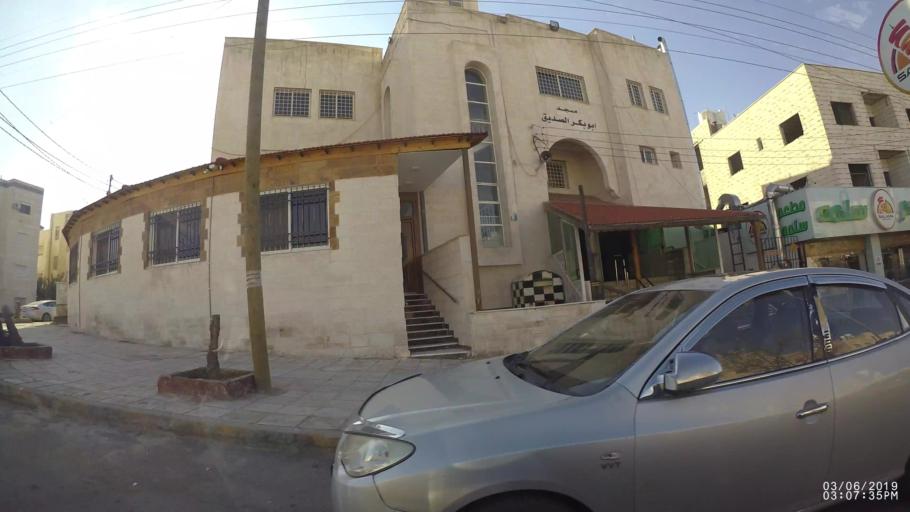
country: JO
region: Amman
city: Amman
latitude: 31.9738
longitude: 35.9386
